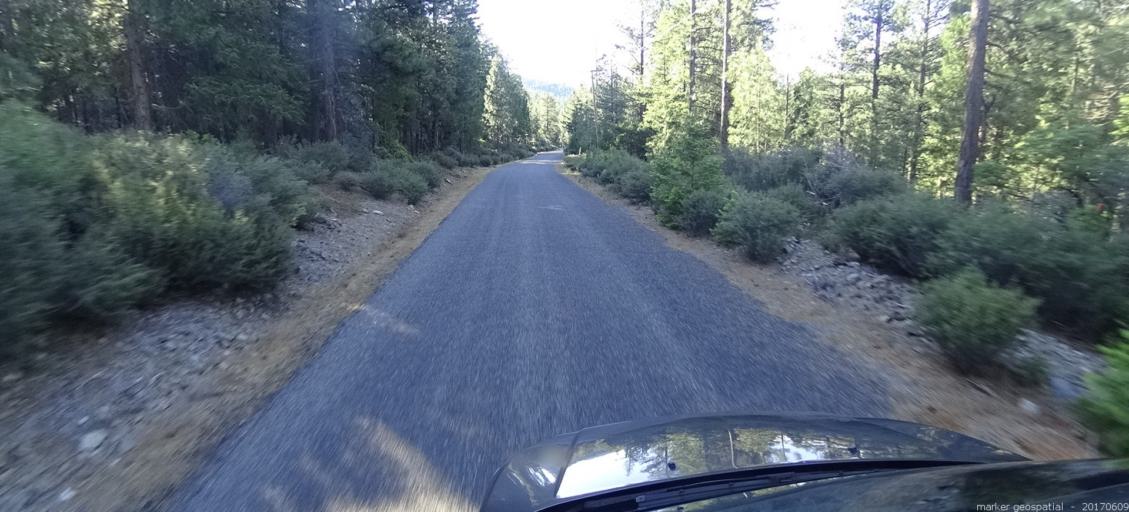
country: US
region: California
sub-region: Siskiyou County
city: Weed
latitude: 41.3800
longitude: -122.6641
